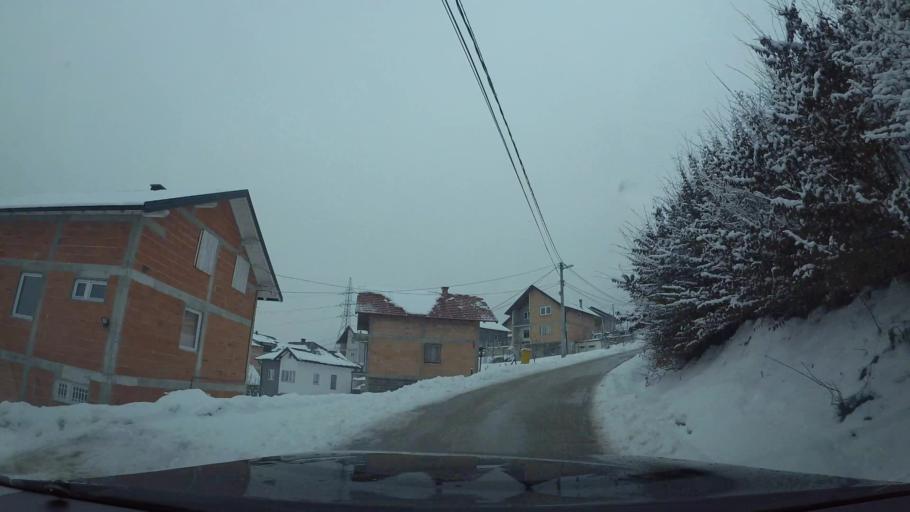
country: BA
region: Federation of Bosnia and Herzegovina
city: Vogosca
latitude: 43.8797
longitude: 18.3180
